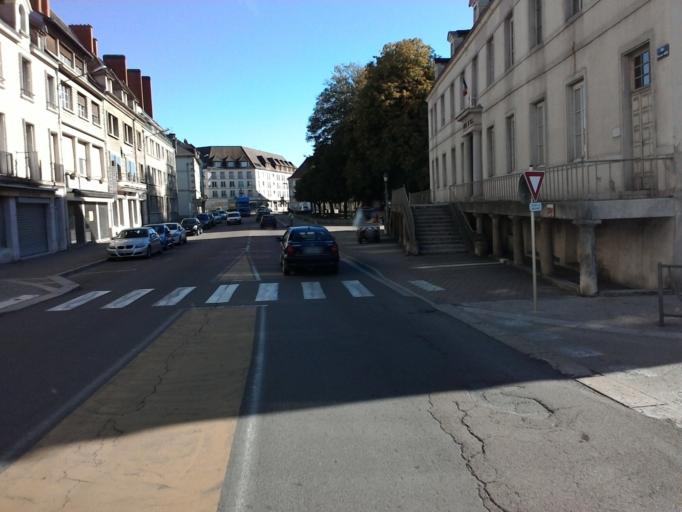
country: FR
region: Bourgogne
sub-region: Departement de la Cote-d'Or
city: Chatillon-sur-Seine
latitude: 47.8604
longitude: 4.5733
